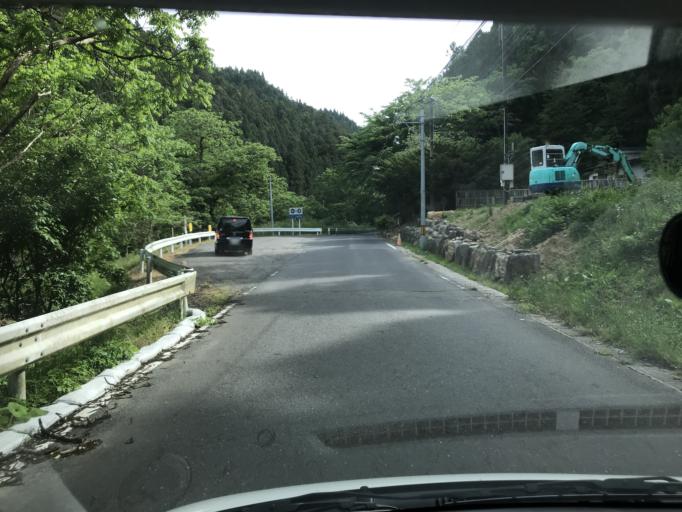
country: JP
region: Miyagi
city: Wakuya
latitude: 38.6712
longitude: 141.3419
